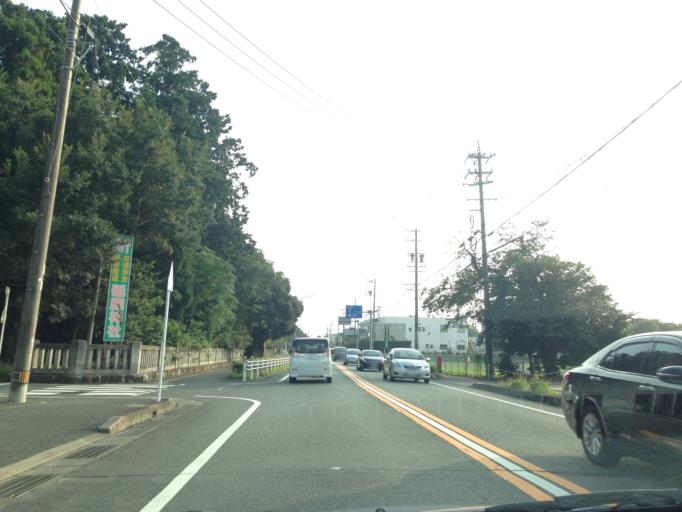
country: JP
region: Aichi
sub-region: Tokai-shi
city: Toyokawa
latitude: 34.8496
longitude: 137.4191
